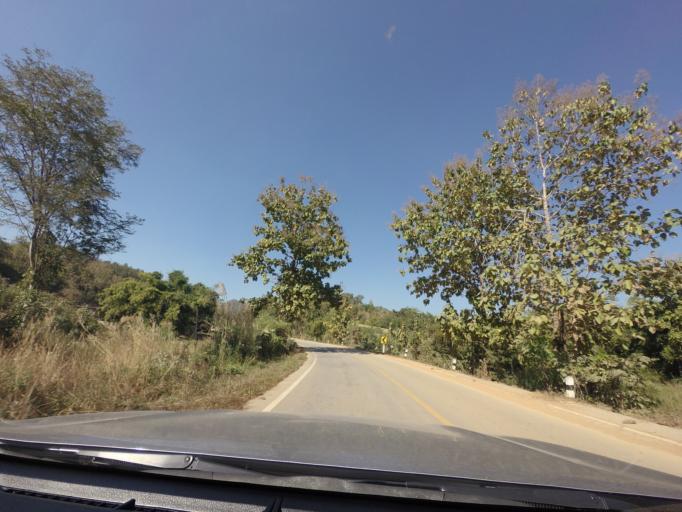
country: TH
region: Lampang
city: Chae Hom
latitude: 18.5350
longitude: 99.6428
